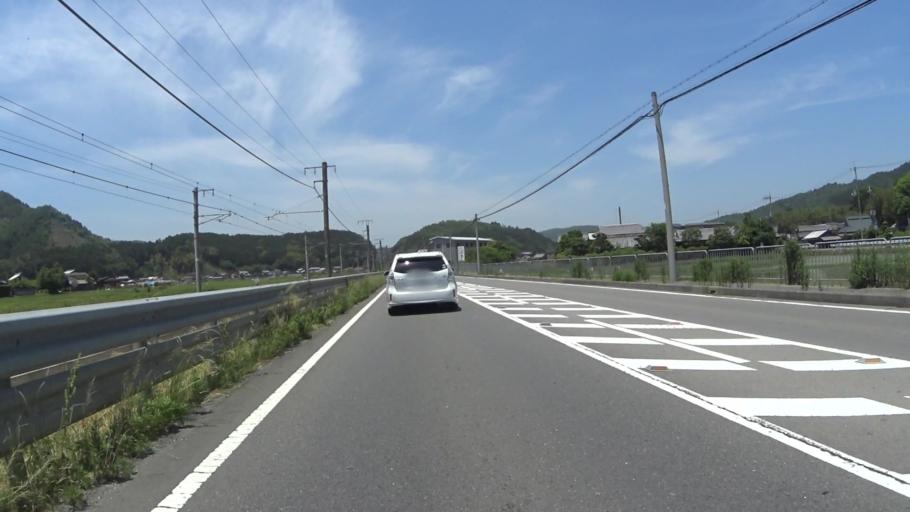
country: JP
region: Kyoto
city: Kameoka
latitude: 35.0763
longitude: 135.5221
